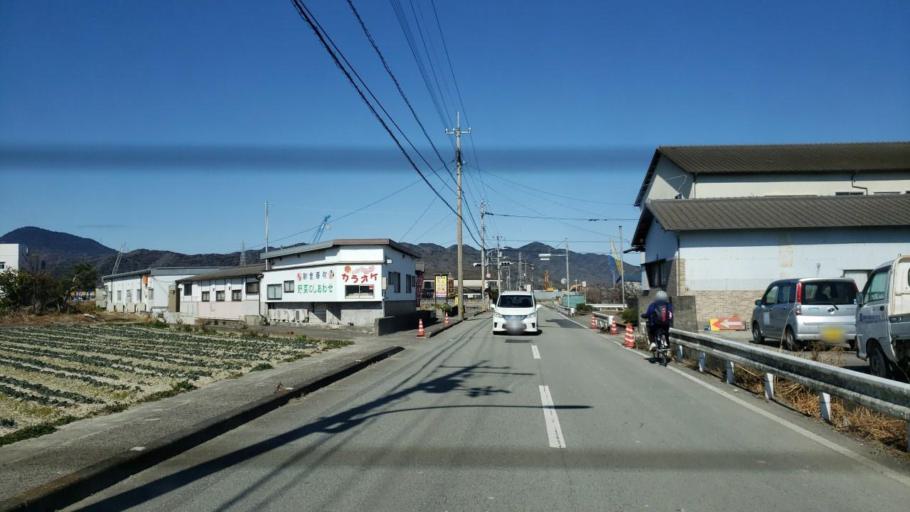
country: JP
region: Tokushima
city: Tokushima-shi
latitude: 34.1393
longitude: 134.5319
